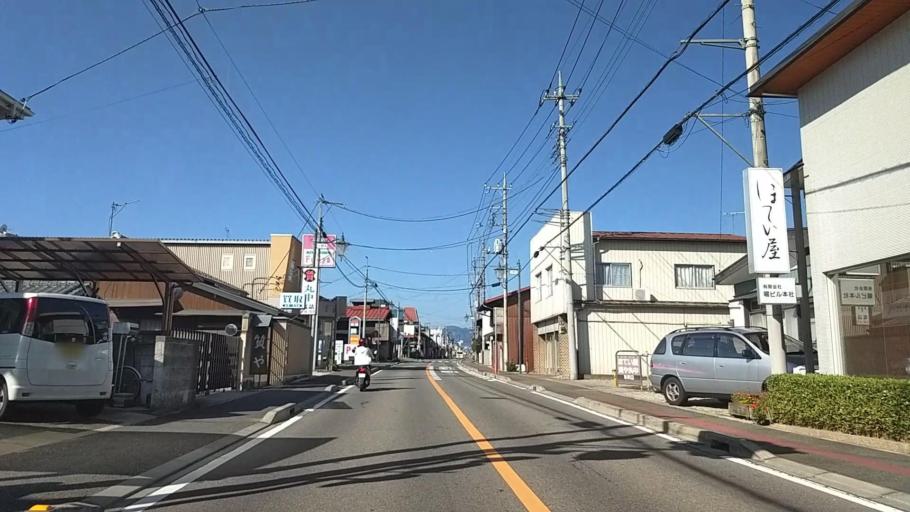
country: JP
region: Gunma
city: Annaka
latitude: 36.3238
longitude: 138.8879
